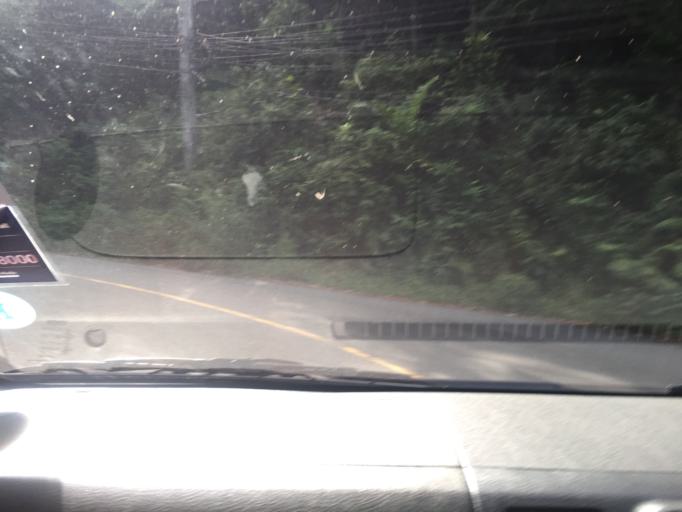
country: TH
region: Trat
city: Laem Ngop
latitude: 12.1234
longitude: 102.2683
